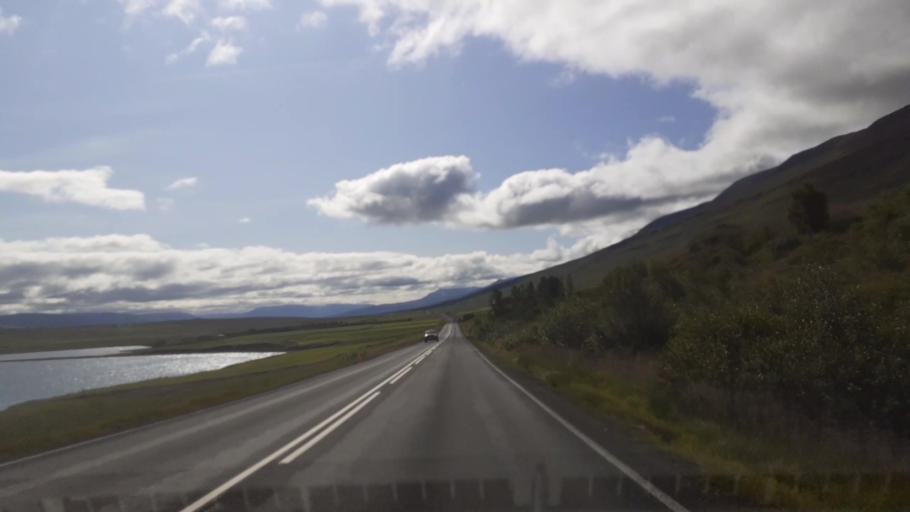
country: IS
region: Northeast
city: Akureyri
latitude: 65.8739
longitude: -18.2640
